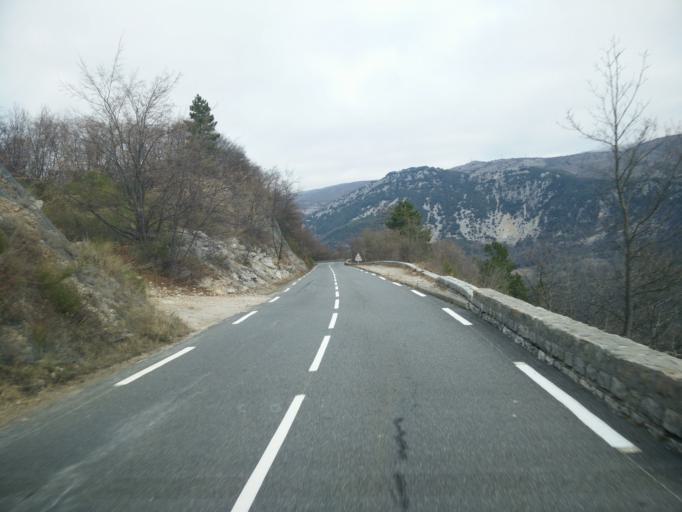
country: FR
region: Provence-Alpes-Cote d'Azur
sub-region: Departement des Alpes-Maritimes
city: Tourrettes-sur-Loup
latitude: 43.7372
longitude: 6.9935
